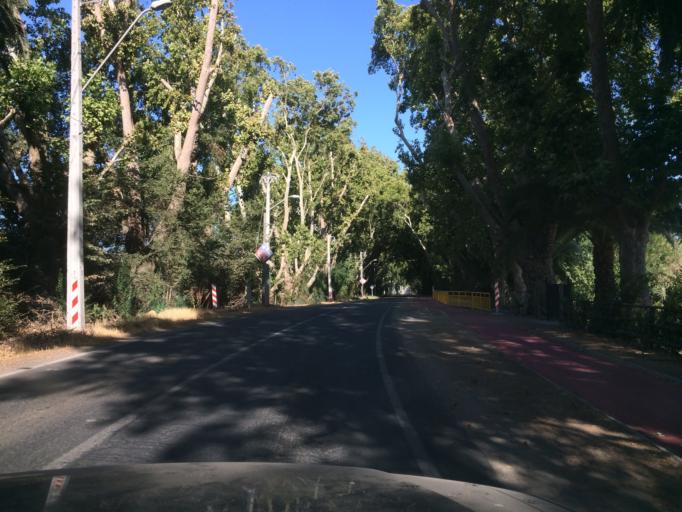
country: CL
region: Santiago Metropolitan
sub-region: Provincia de Melipilla
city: Melipilla
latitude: -33.4886
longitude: -71.1847
